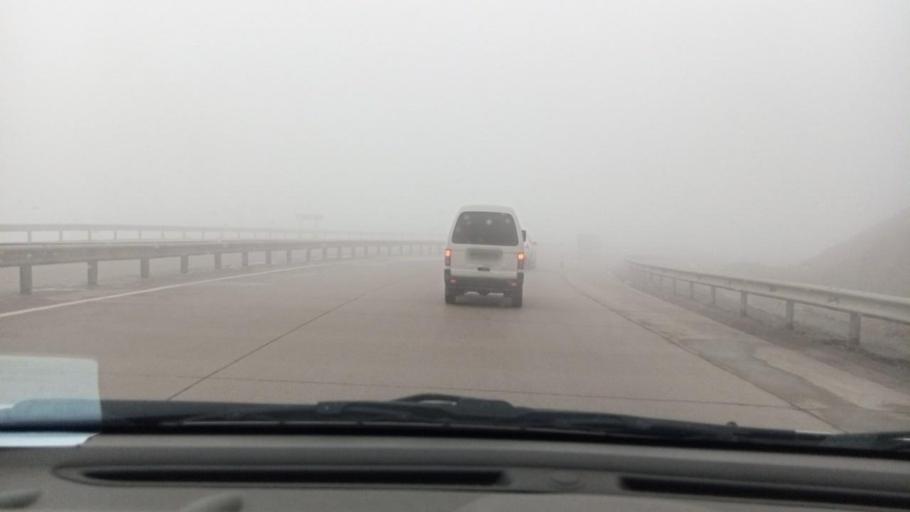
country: UZ
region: Toshkent
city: Angren
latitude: 41.1050
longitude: 70.5109
